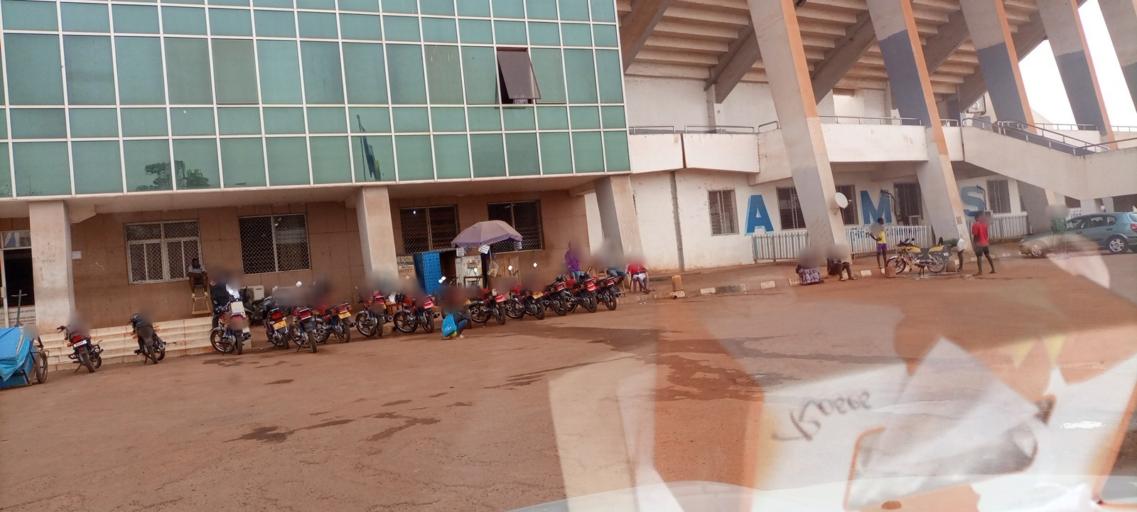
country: CF
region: Bangui
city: Bangui
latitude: 4.3743
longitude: 18.5633
